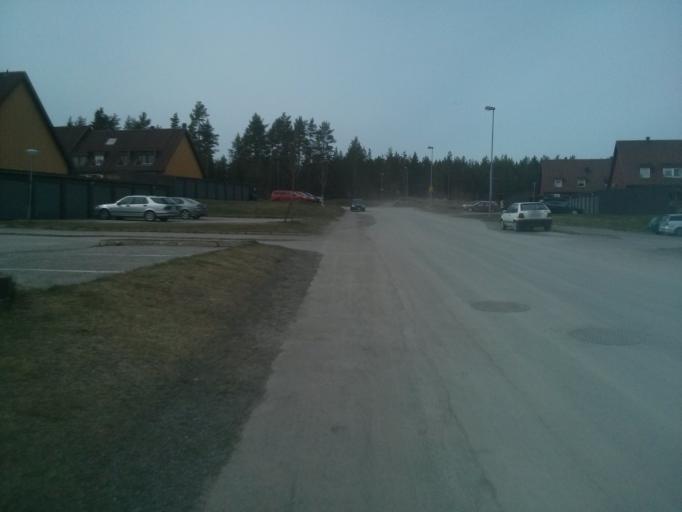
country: SE
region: Vaesternorrland
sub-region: Haernoesands Kommun
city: Haernoesand
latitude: 62.6359
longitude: 17.9087
